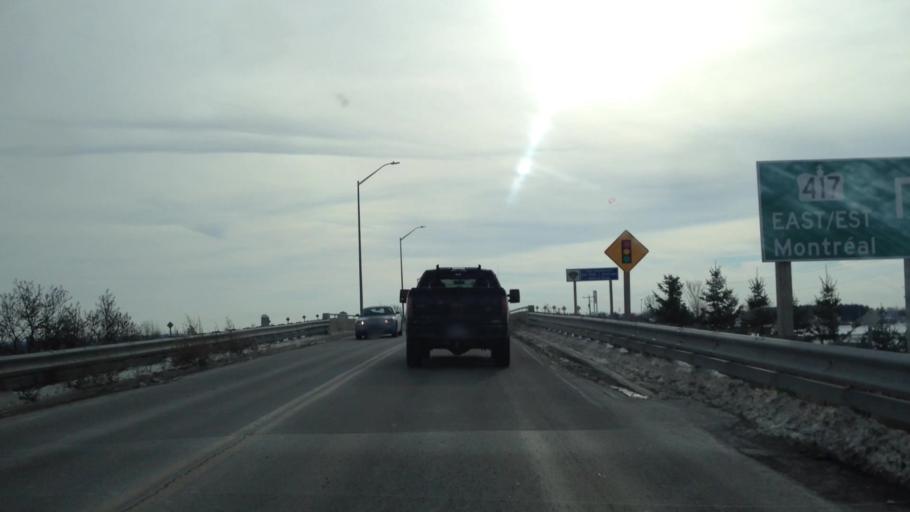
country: CA
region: Ontario
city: Casselman
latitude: 45.3039
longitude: -75.0806
